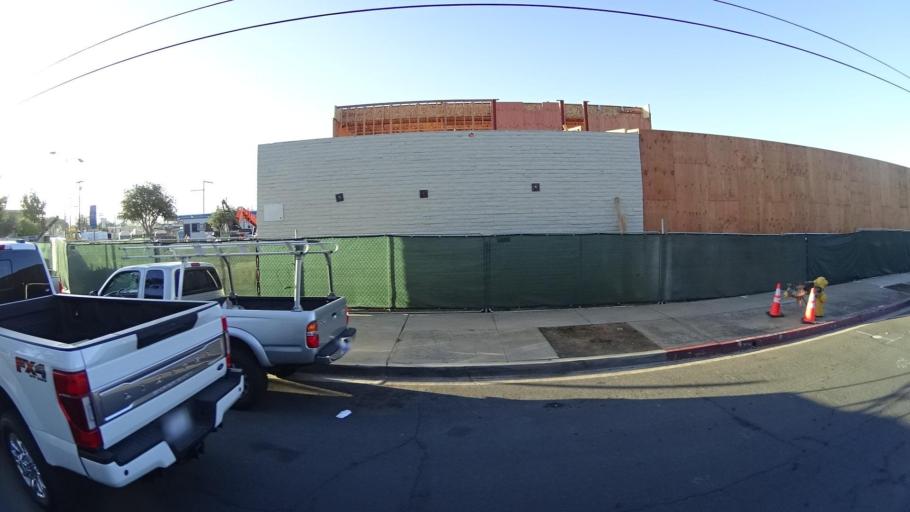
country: US
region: California
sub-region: San Diego County
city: Bostonia
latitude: 32.8089
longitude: -116.9366
